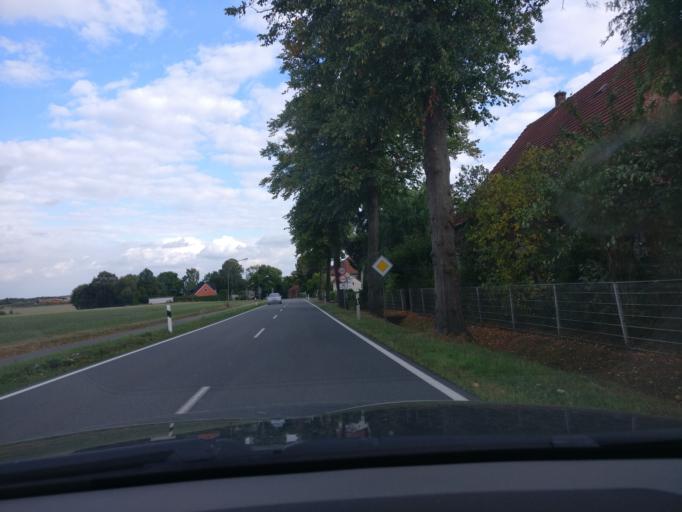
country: DE
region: Lower Saxony
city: Melle
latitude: 52.1889
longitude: 8.3569
